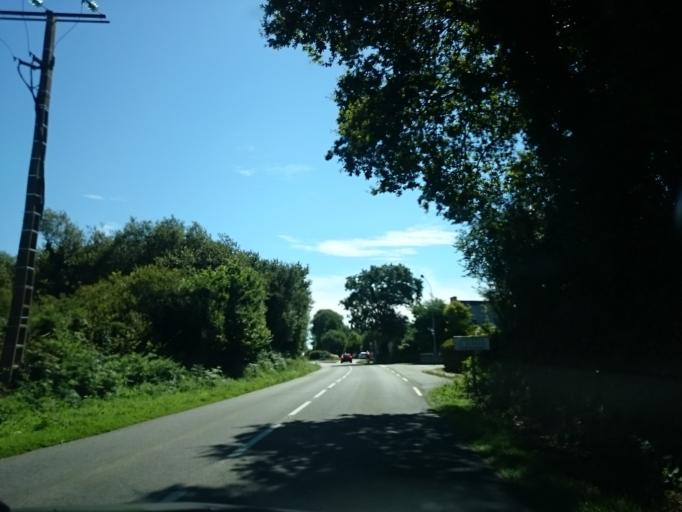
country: FR
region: Brittany
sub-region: Departement du Finistere
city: Saint-Renan
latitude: 48.4384
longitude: -4.6355
